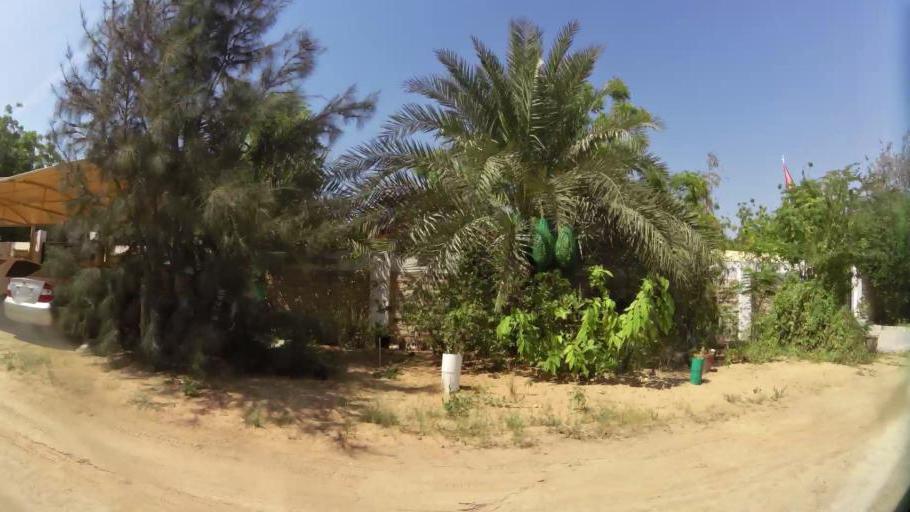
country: AE
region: Ajman
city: Ajman
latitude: 25.4147
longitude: 55.4749
